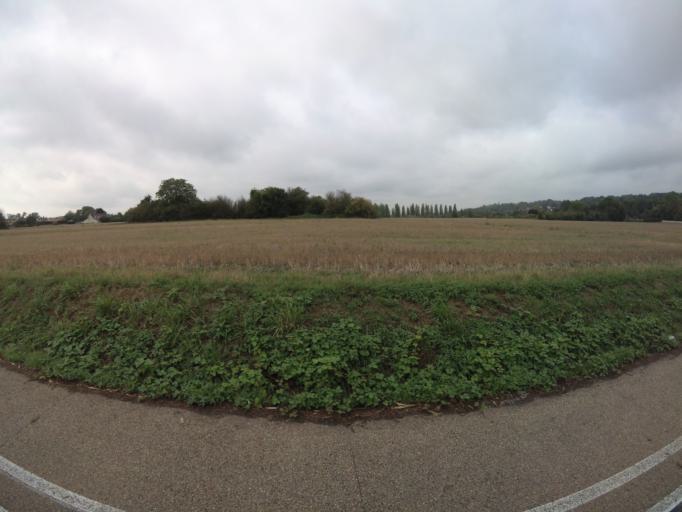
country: FR
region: Ile-de-France
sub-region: Departement de Seine-et-Marne
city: Guermantes
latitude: 48.8580
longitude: 2.7037
